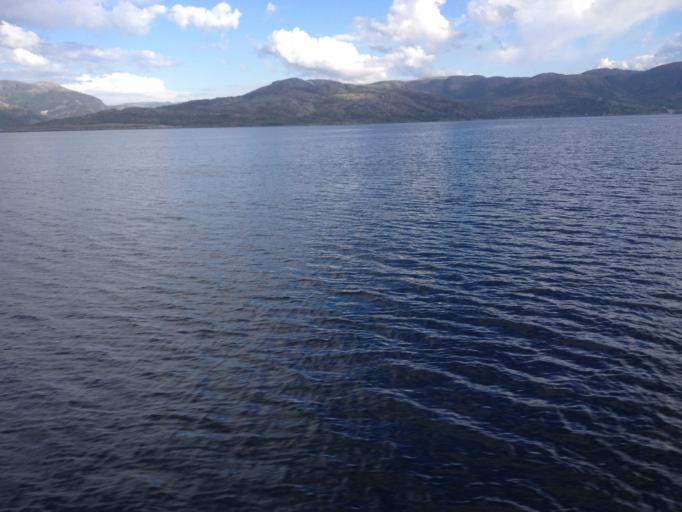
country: NO
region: Sor-Trondelag
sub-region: Hitra
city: Fillan
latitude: 63.5305
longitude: 9.1962
